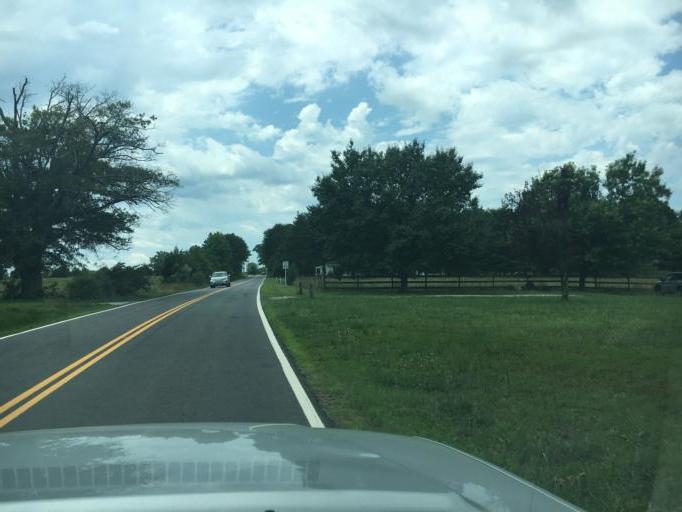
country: US
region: South Carolina
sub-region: Spartanburg County
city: Duncan
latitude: 34.8760
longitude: -82.1776
